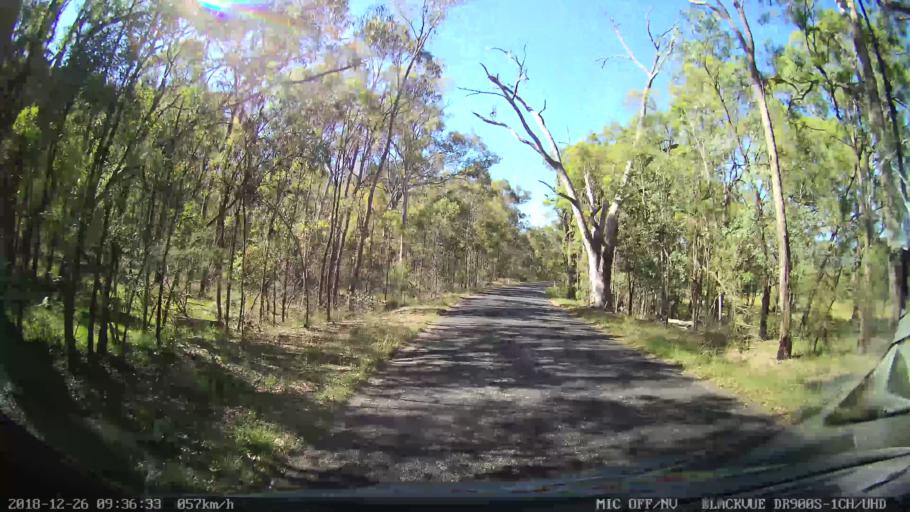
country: AU
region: New South Wales
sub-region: Mid-Western Regional
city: Kandos
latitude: -32.9248
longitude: 150.0400
